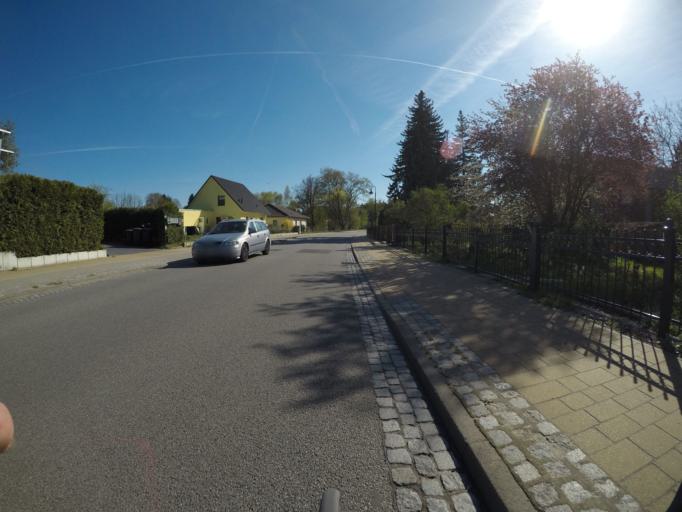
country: DE
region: Brandenburg
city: Rehfelde
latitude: 52.4584
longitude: 13.9096
